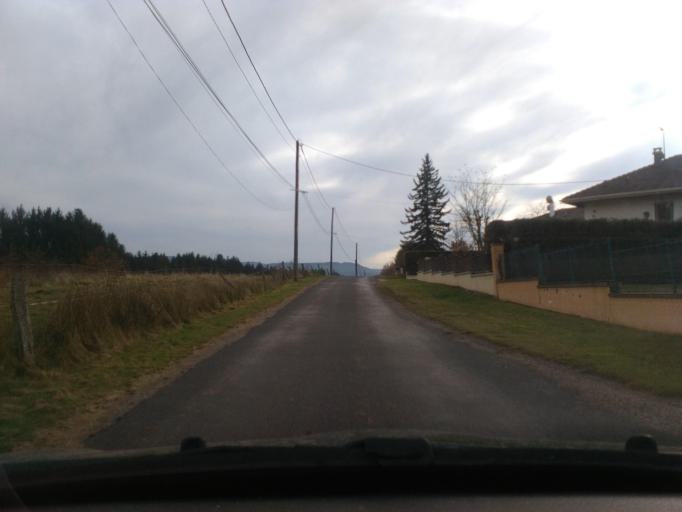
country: FR
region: Lorraine
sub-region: Departement des Vosges
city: Sainte-Marguerite
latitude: 48.2872
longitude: 7.0184
